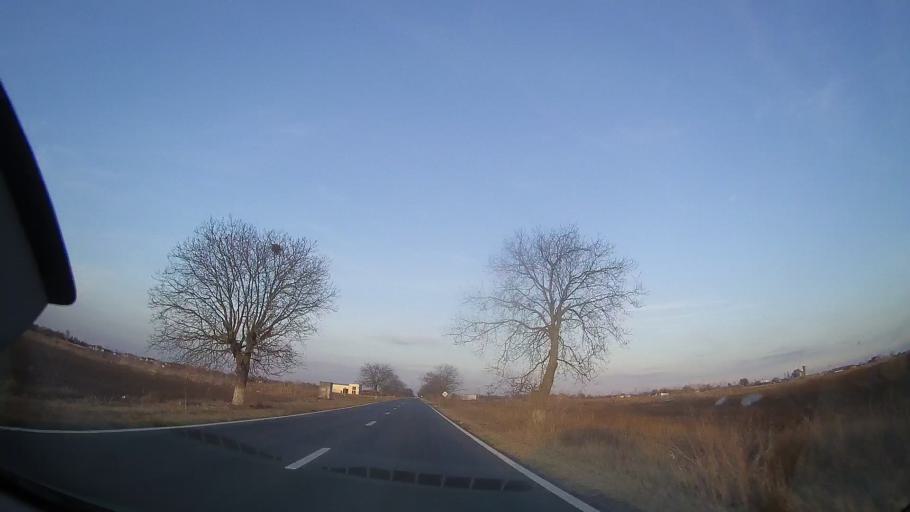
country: RO
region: Constanta
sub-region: Comuna Topraisar
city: Topraisar
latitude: 44.0044
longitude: 28.4395
